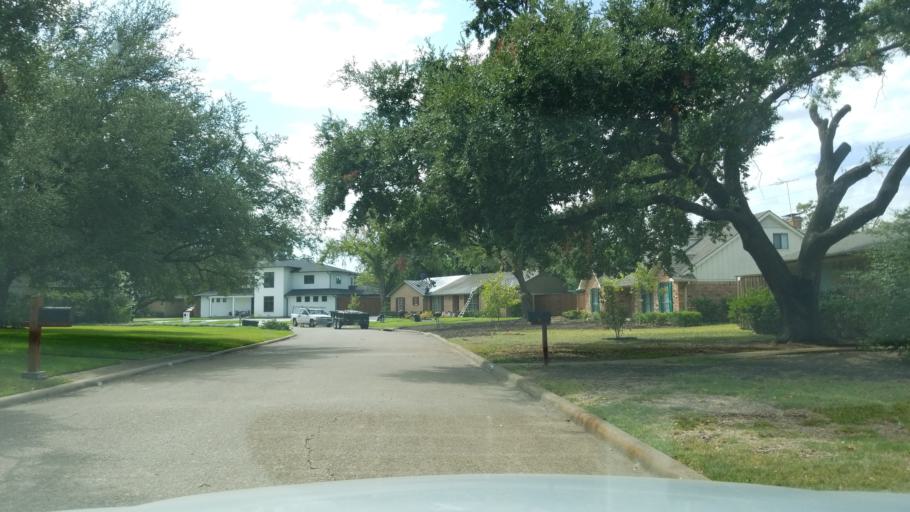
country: US
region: Texas
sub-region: Dallas County
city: Richardson
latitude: 32.9523
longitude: -96.7776
